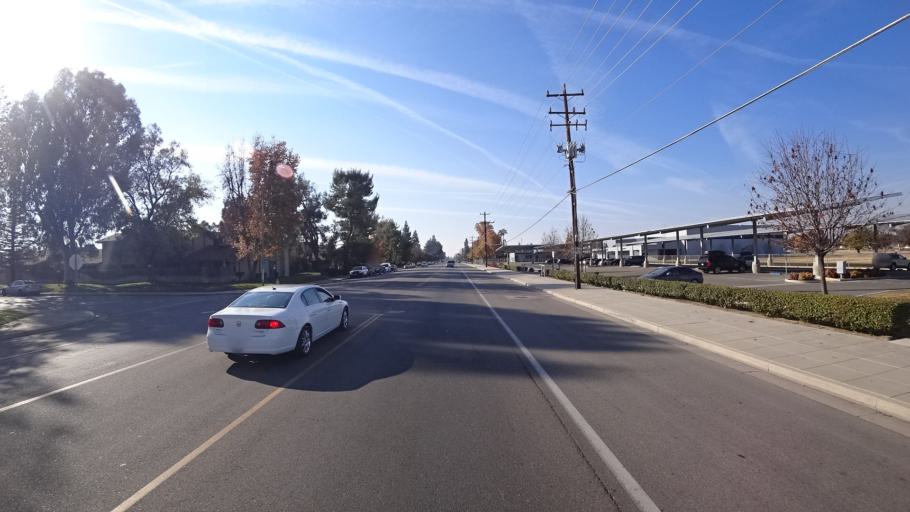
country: US
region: California
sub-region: Kern County
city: Bakersfield
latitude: 35.3251
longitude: -119.0492
